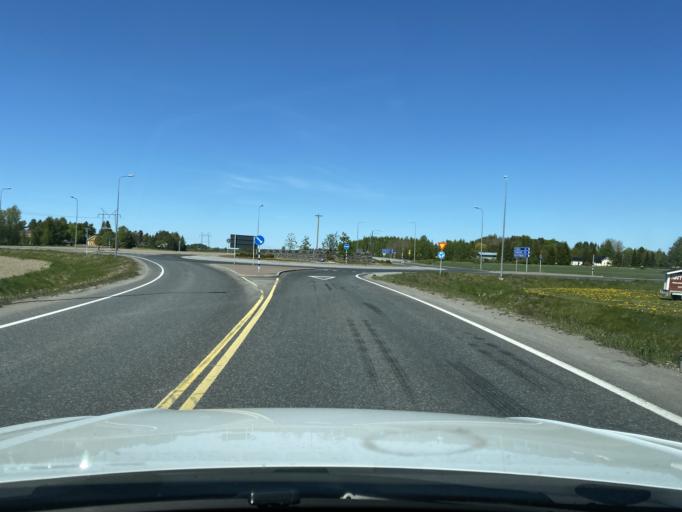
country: FI
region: Satakunta
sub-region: Rauma
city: Eura
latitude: 61.1307
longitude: 22.1246
